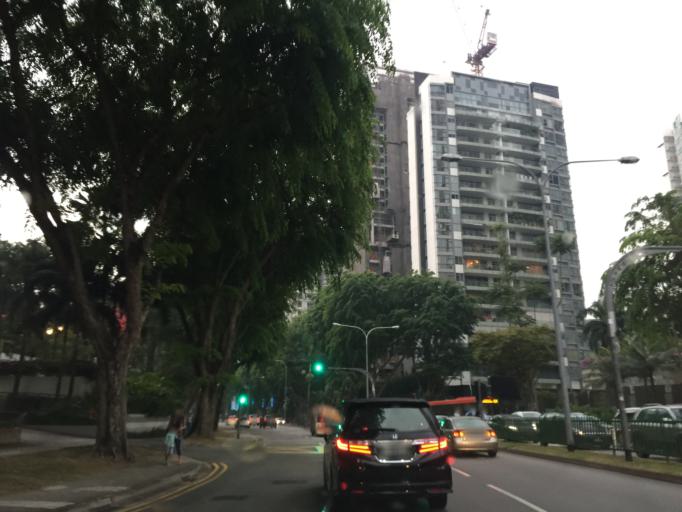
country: SG
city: Singapore
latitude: 1.3146
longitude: 103.8406
